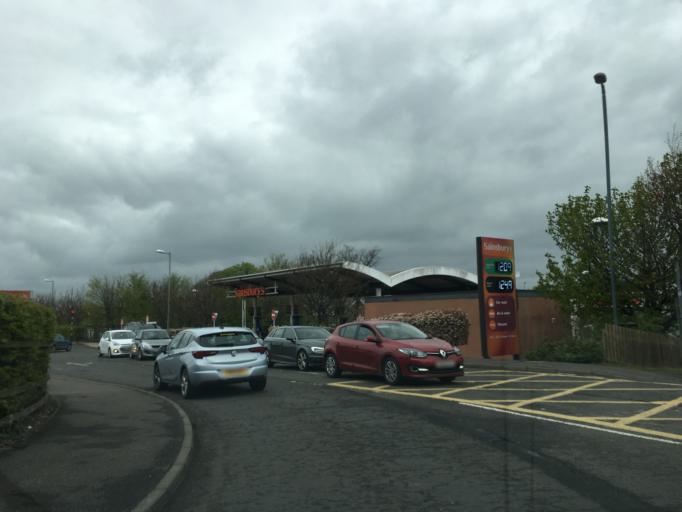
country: GB
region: Scotland
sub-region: Stirling
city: Stirling
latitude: 56.1284
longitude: -3.9433
